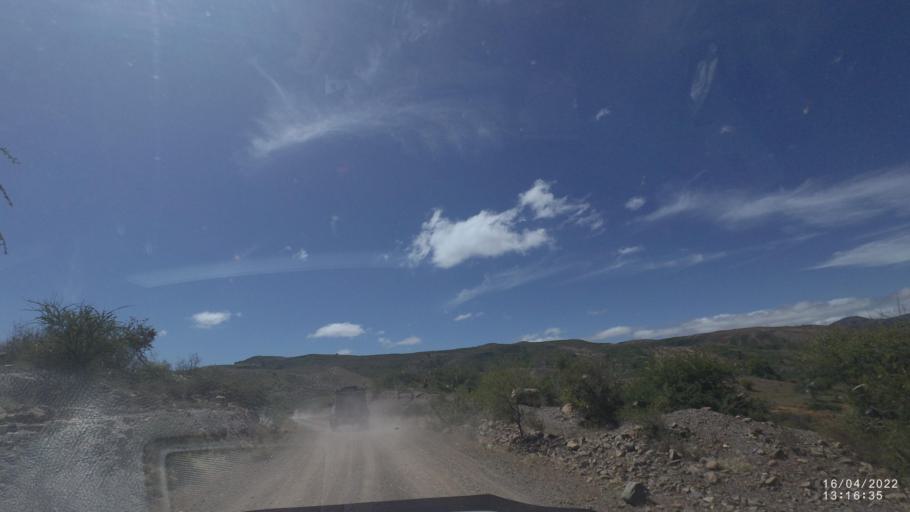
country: BO
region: Cochabamba
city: Mizque
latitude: -17.9880
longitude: -65.6237
